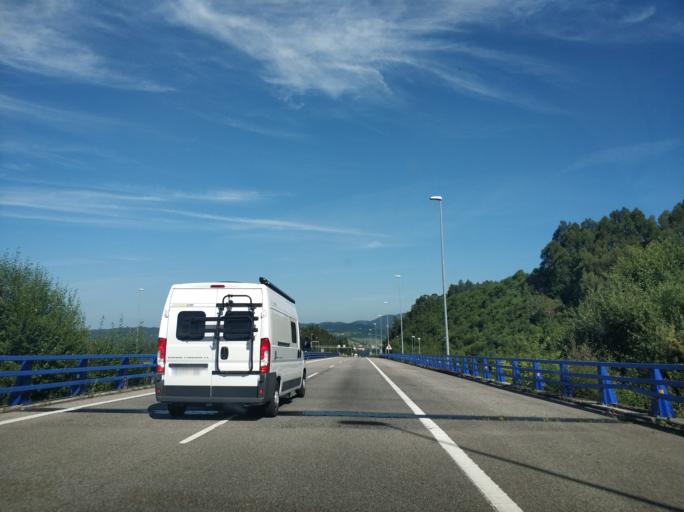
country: ES
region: Asturias
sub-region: Province of Asturias
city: Muros de Nalon
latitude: 43.5369
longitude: -6.1118
